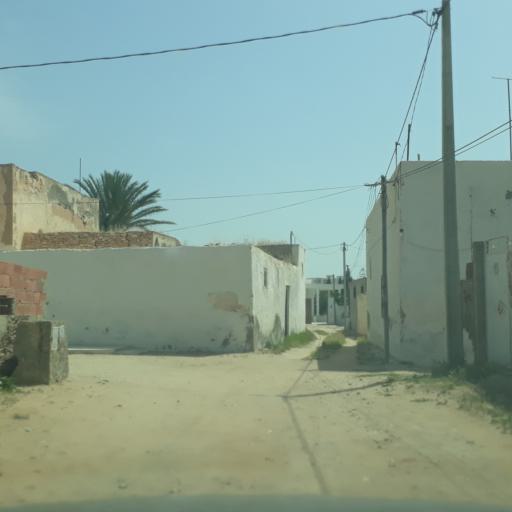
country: TN
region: Safaqis
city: Al Qarmadah
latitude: 34.7983
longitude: 10.7642
